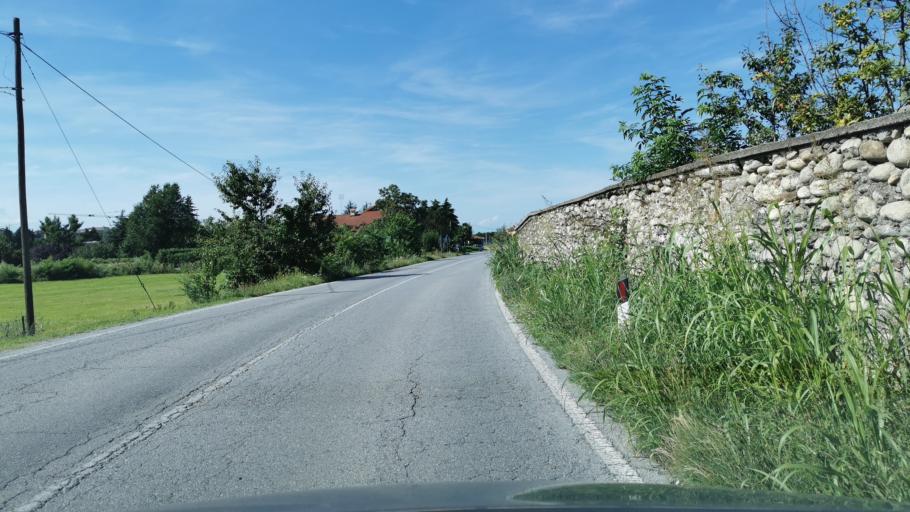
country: IT
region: Piedmont
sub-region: Provincia di Cuneo
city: Cuneo
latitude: 44.3766
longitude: 7.5574
